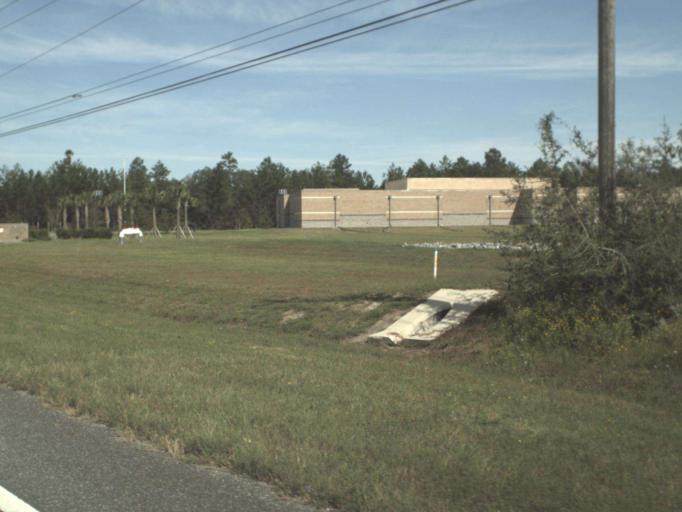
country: US
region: Florida
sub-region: Bay County
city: Lynn Haven
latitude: 30.3769
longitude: -85.6785
